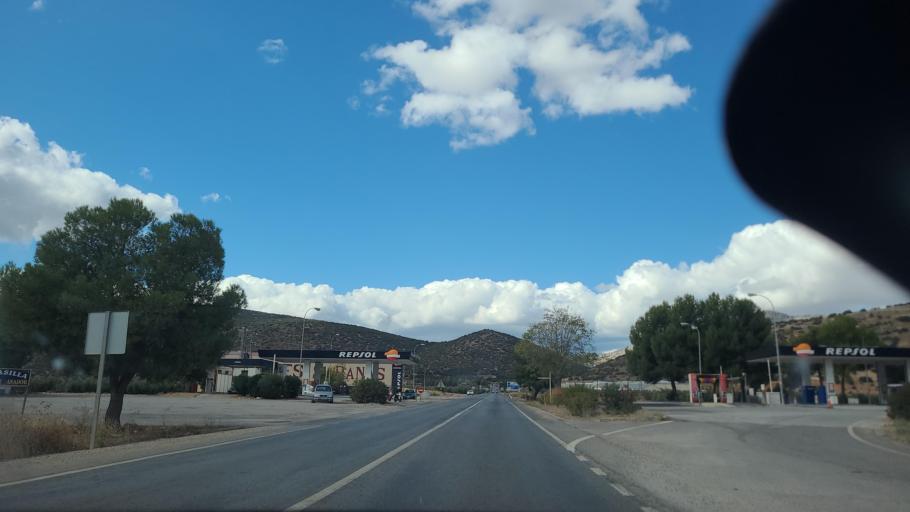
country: ES
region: Andalusia
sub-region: Provincia de Granada
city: Iznalloz
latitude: 37.4005
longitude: -3.5537
